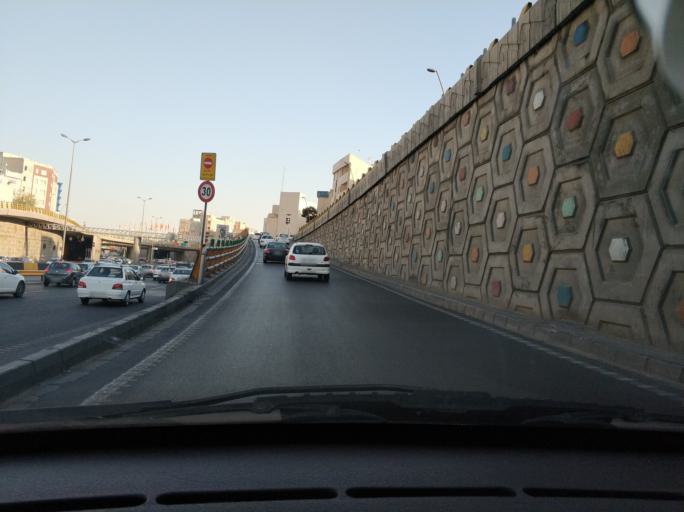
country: IR
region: Tehran
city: Tehran
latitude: 35.6893
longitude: 51.4569
